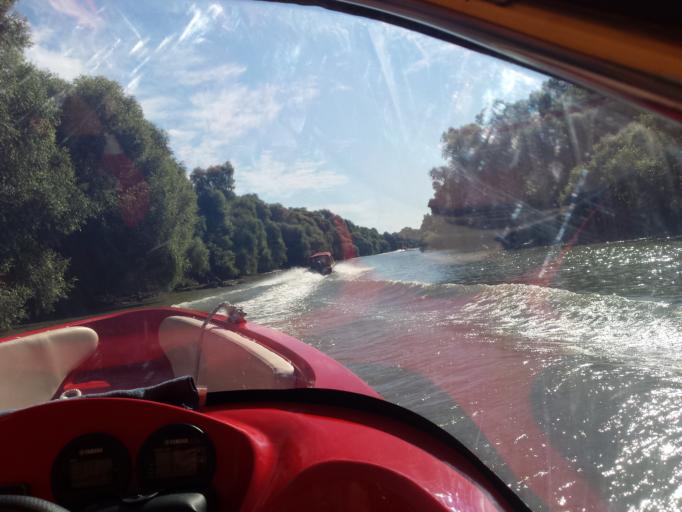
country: RO
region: Tulcea
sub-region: Comuna Pardina
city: Pardina
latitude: 45.2537
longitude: 28.9545
